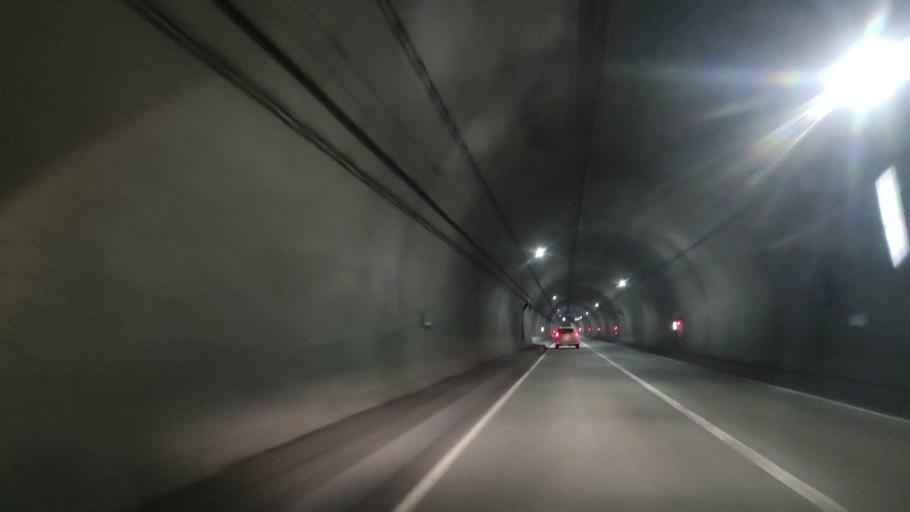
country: JP
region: Hokkaido
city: Rumoi
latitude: 43.7141
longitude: 141.3305
